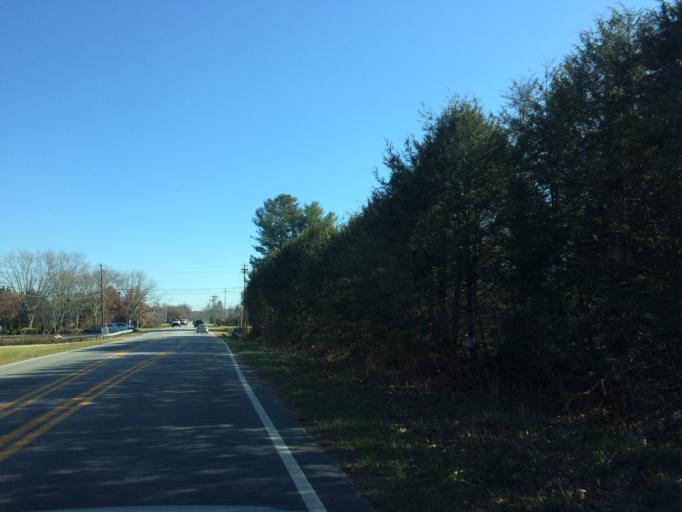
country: US
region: North Carolina
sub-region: Henderson County
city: Mills River
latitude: 35.3811
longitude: -82.5525
